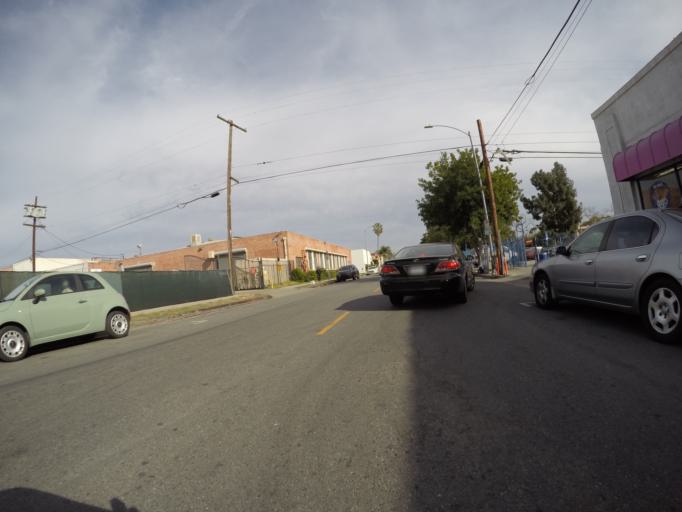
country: US
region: California
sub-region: Los Angeles County
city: West Hollywood
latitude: 34.0871
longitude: -118.3436
